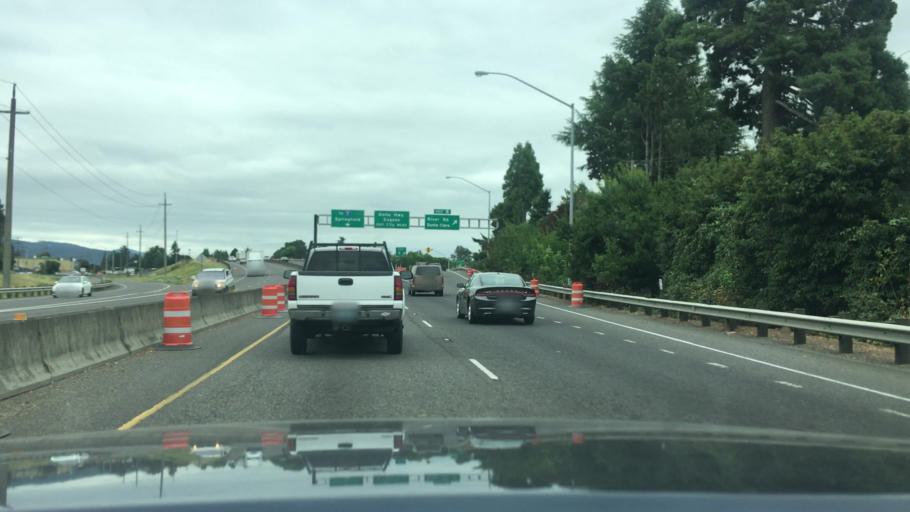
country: US
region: Oregon
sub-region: Lane County
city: Eugene
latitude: 44.0974
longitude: -123.1334
